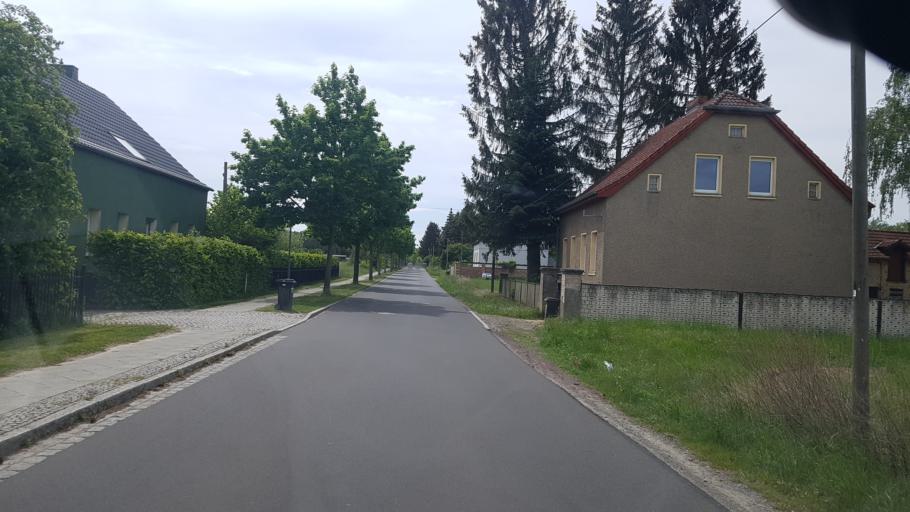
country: DE
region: Brandenburg
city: Michendorf
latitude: 52.3102
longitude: 13.0628
